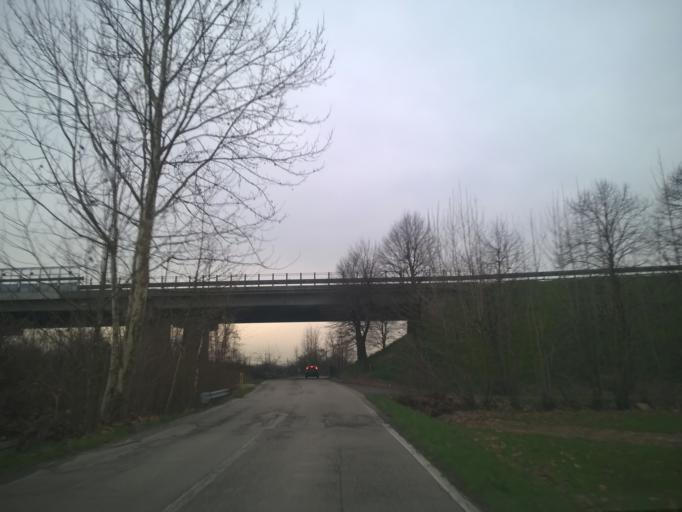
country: IT
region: Veneto
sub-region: Provincia di Vicenza
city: Lisiera
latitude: 45.5756
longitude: 11.6052
